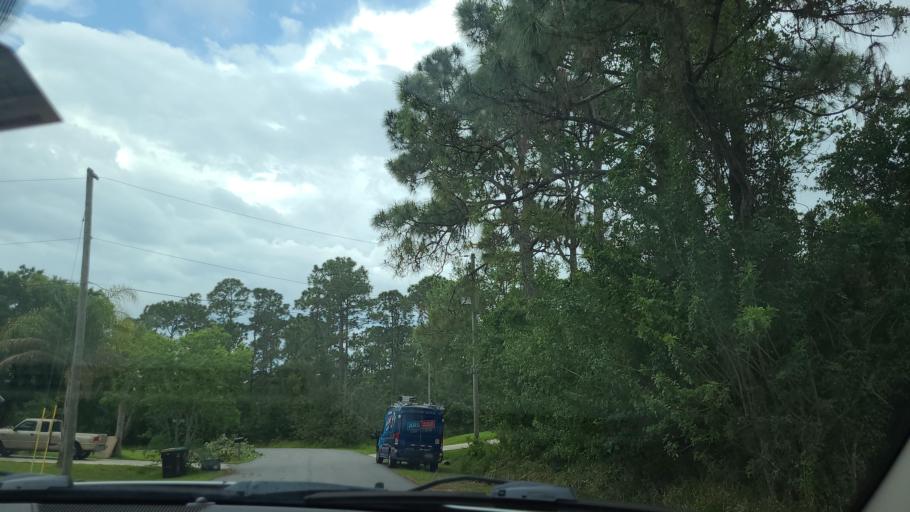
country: US
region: Florida
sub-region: Brevard County
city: Grant-Valkaria
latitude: 27.9413
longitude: -80.6375
